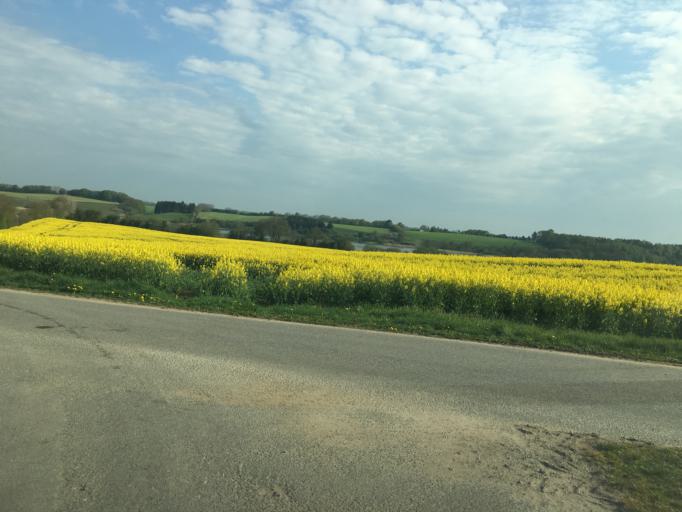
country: DK
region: South Denmark
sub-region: Haderslev Kommune
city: Vojens
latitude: 55.1845
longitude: 9.3947
